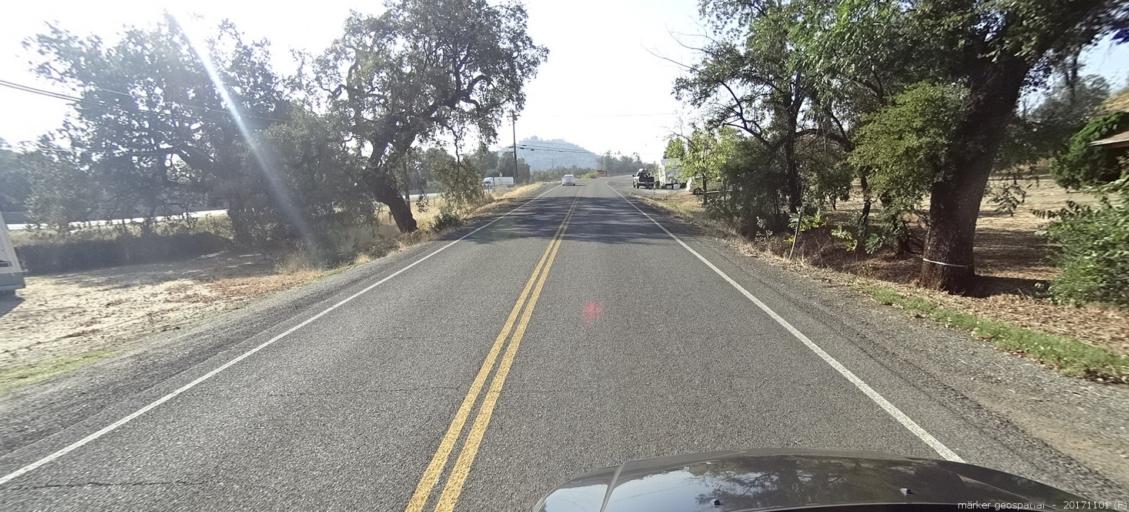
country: US
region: California
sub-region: Shasta County
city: Shasta Lake
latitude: 40.7177
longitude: -122.3308
